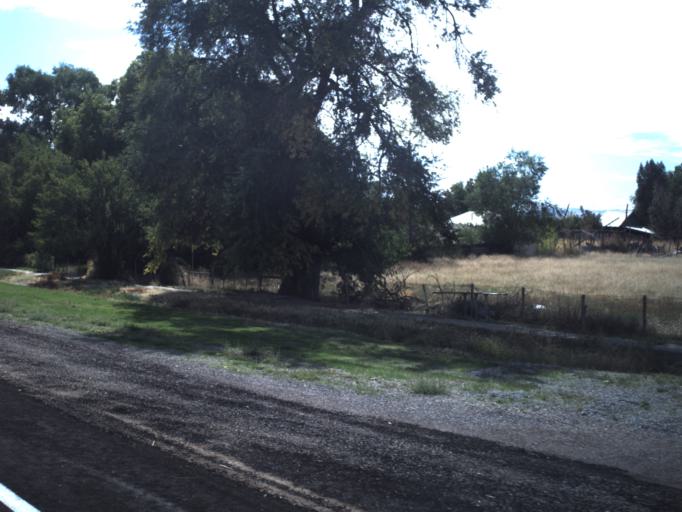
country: US
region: Utah
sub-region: Millard County
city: Fillmore
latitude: 38.8855
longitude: -112.4106
